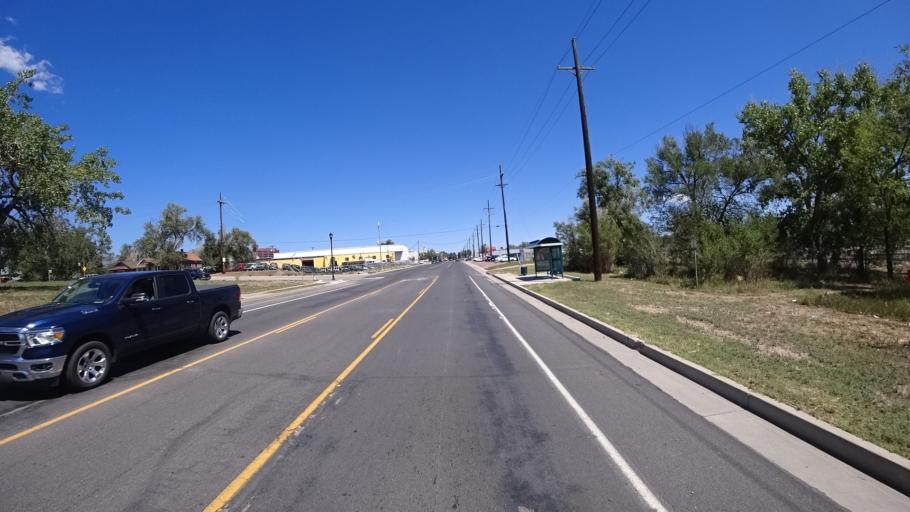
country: US
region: Colorado
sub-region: El Paso County
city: Colorado Springs
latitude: 38.8240
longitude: -104.8185
